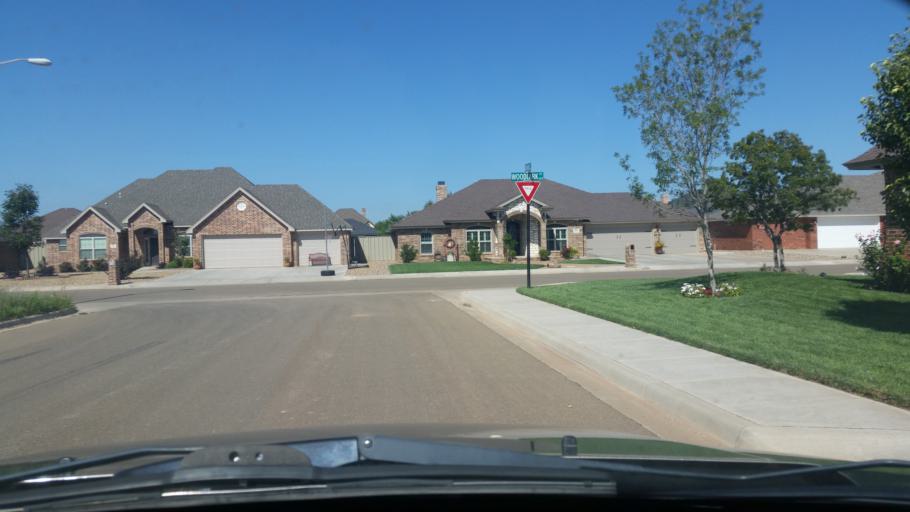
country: US
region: New Mexico
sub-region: Curry County
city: Clovis
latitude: 34.4380
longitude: -103.1730
